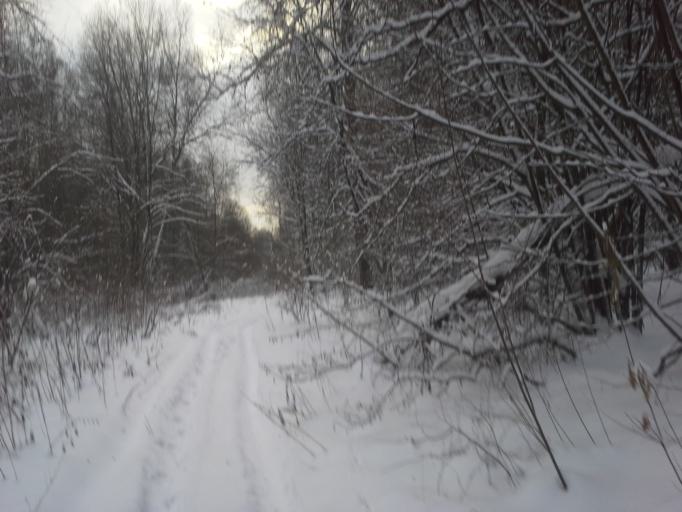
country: RU
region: Moscow
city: Yasenevo
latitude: 55.5905
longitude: 37.5059
